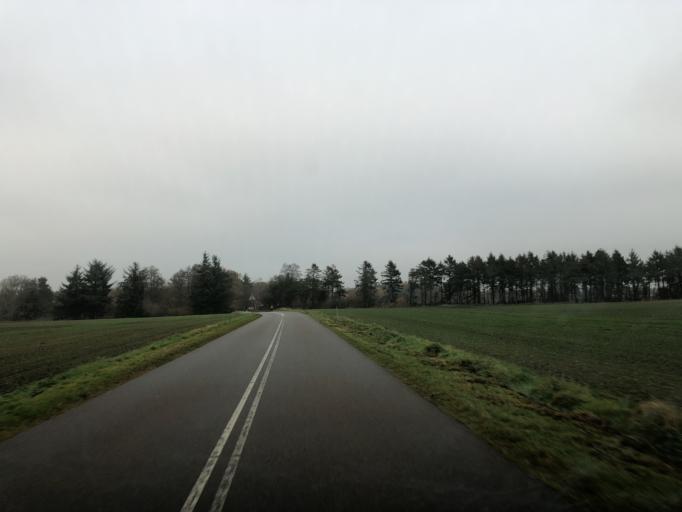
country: DK
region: Central Jutland
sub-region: Herning Kommune
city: Avlum
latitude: 56.2441
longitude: 8.8812
